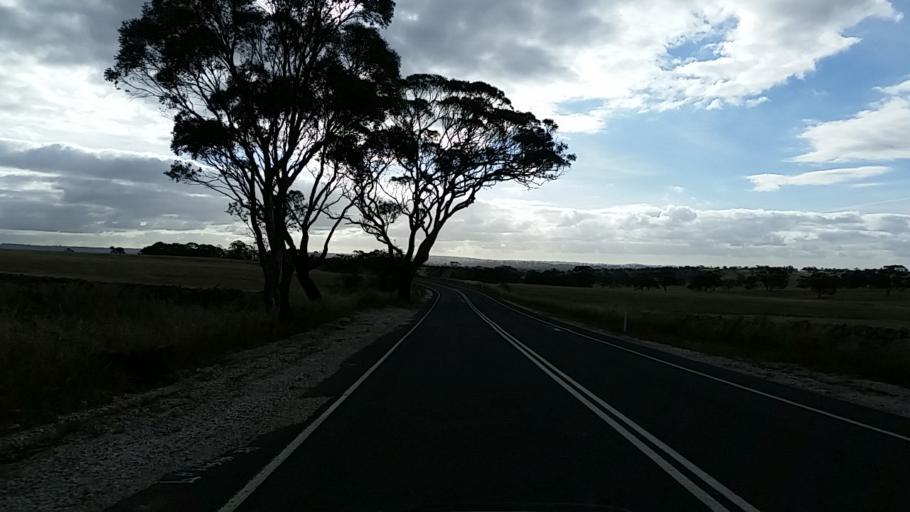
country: AU
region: South Australia
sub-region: Barossa
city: Angaston
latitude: -34.5613
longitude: 139.1921
